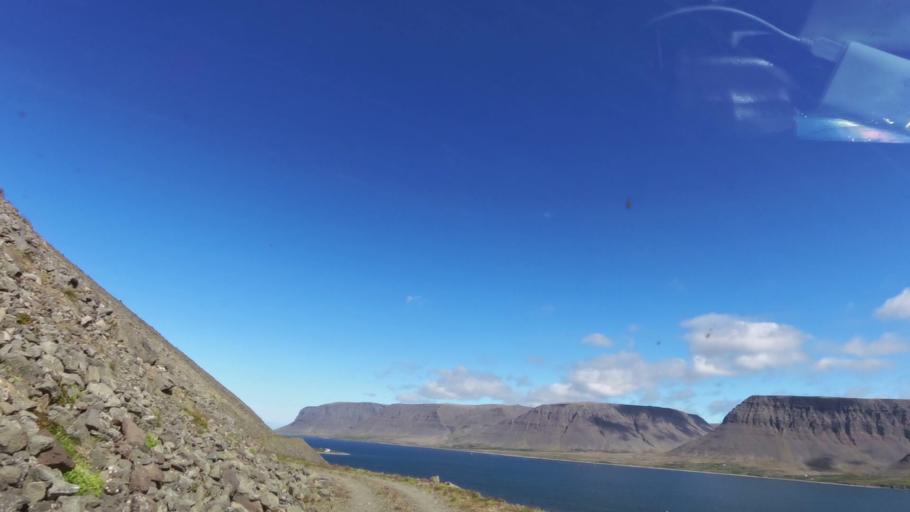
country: IS
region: West
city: Olafsvik
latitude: 65.6311
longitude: -23.9147
